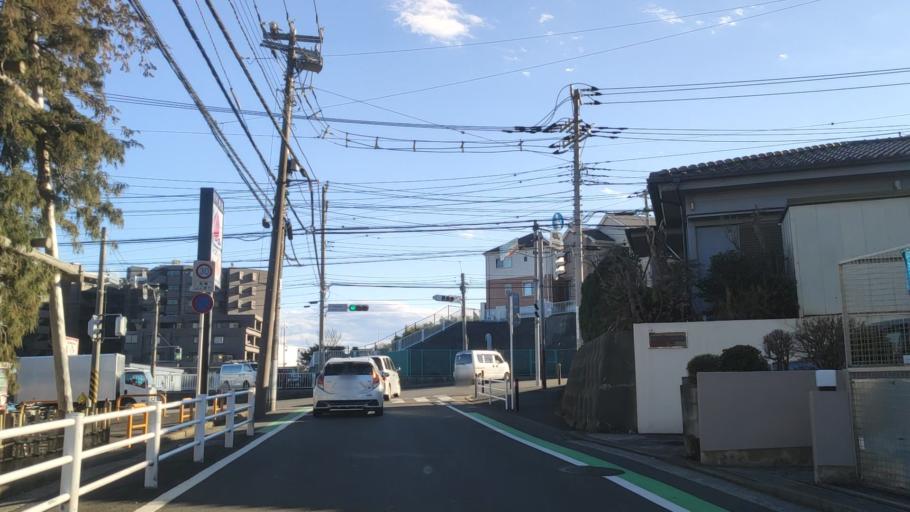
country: JP
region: Tokyo
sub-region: Machida-shi
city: Machida
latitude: 35.5131
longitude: 139.5483
